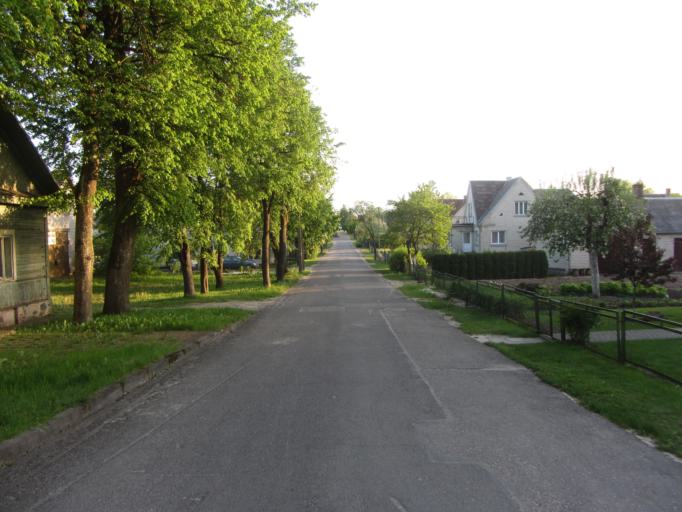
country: LT
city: Sirvintos
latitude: 55.0365
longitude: 24.9675
